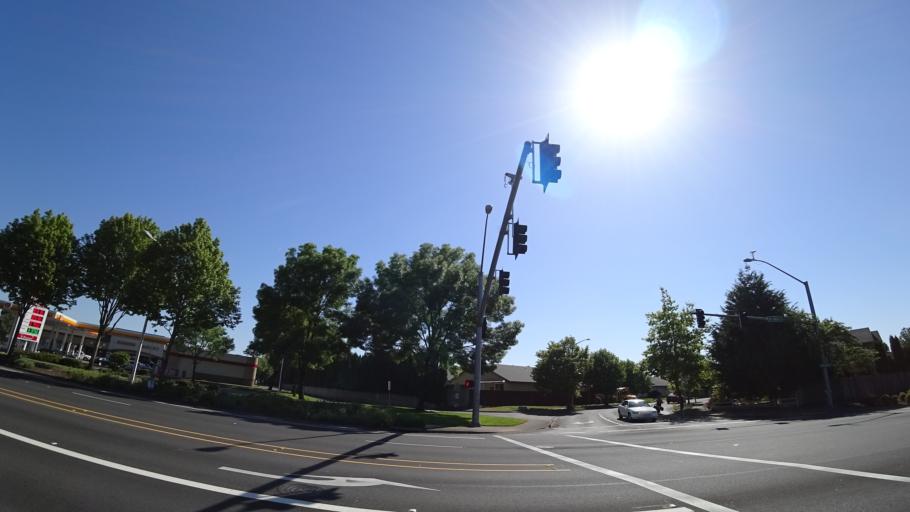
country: US
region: Oregon
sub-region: Washington County
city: Rockcreek
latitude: 45.5166
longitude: -122.9043
